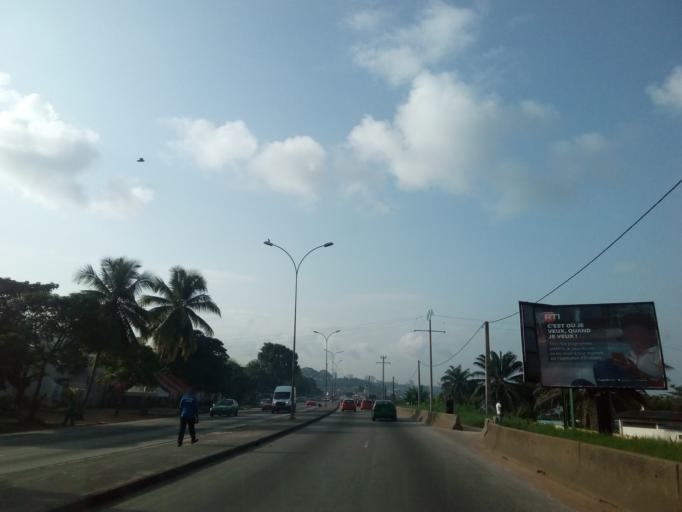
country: CI
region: Lagunes
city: Abidjan
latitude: 5.3450
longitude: -4.0383
